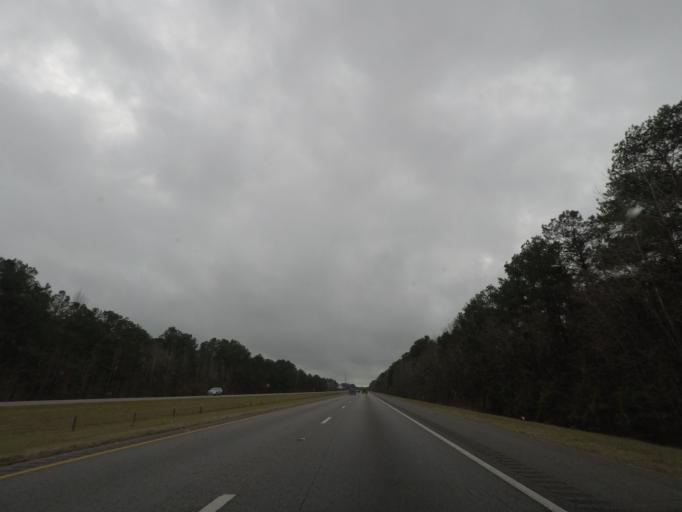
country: US
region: South Carolina
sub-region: Orangeburg County
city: Holly Hill
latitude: 33.4362
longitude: -80.4858
